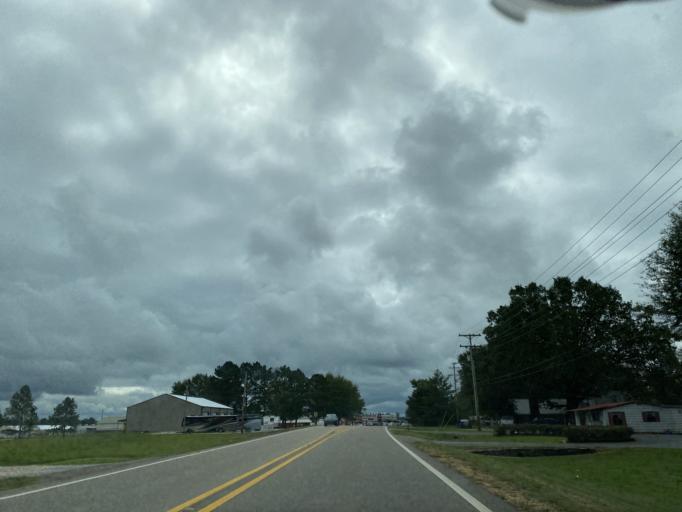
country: US
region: Mississippi
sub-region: Tishomingo County
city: Belmont
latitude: 34.4904
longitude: -88.2075
